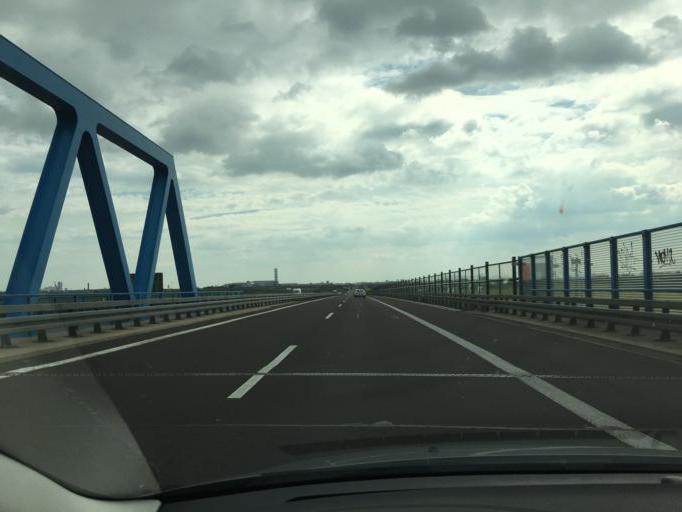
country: DE
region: Saxony-Anhalt
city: Ilberstedt
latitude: 51.8086
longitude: 11.6695
